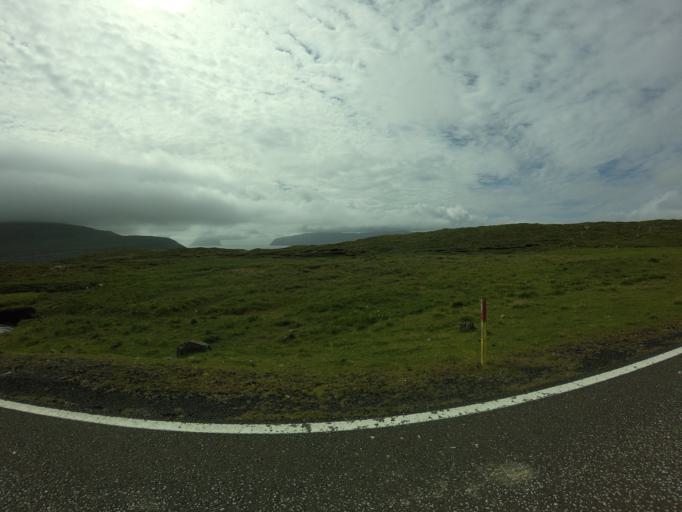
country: FO
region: Sandoy
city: Sandur
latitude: 61.8284
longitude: -6.7566
